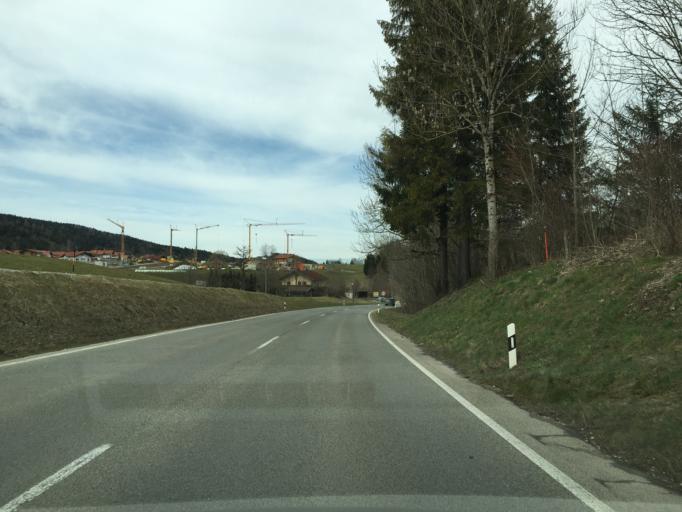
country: DE
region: Bavaria
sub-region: Upper Bavaria
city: Inzell
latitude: 47.7825
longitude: 12.7337
